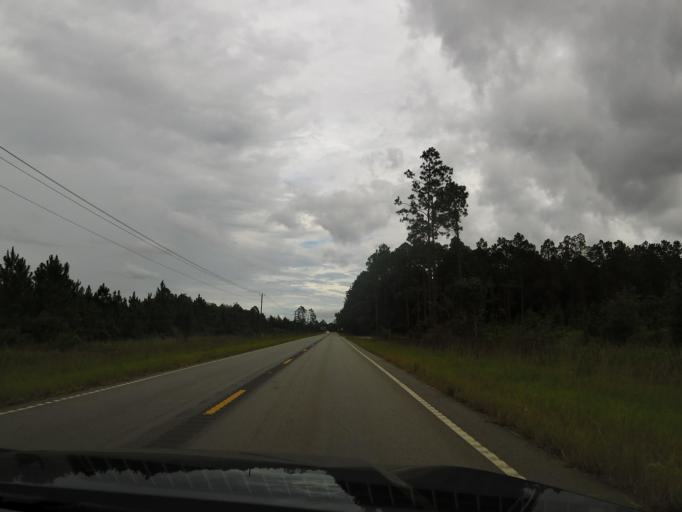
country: US
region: Florida
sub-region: Baker County
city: Macclenny
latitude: 30.5174
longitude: -82.1017
